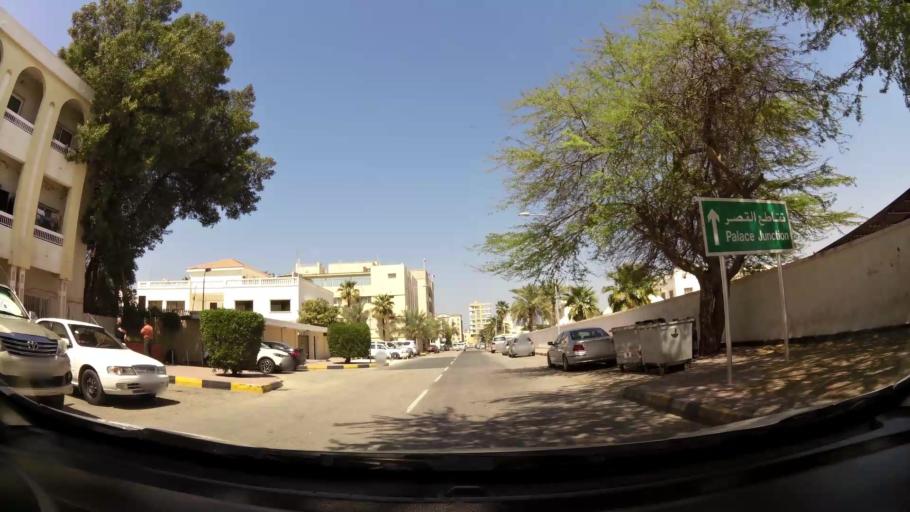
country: BH
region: Manama
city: Manama
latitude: 26.2211
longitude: 50.5913
